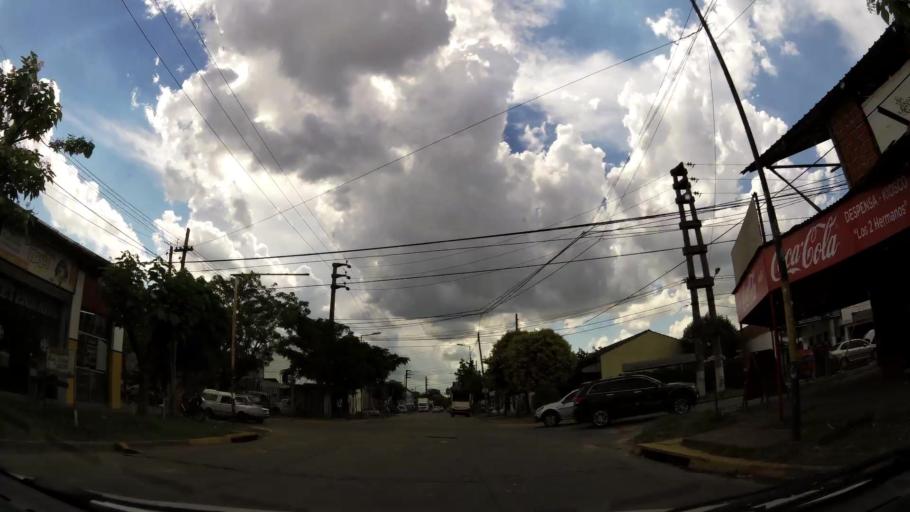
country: AR
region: Buenos Aires
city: Ituzaingo
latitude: -34.6365
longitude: -58.6673
